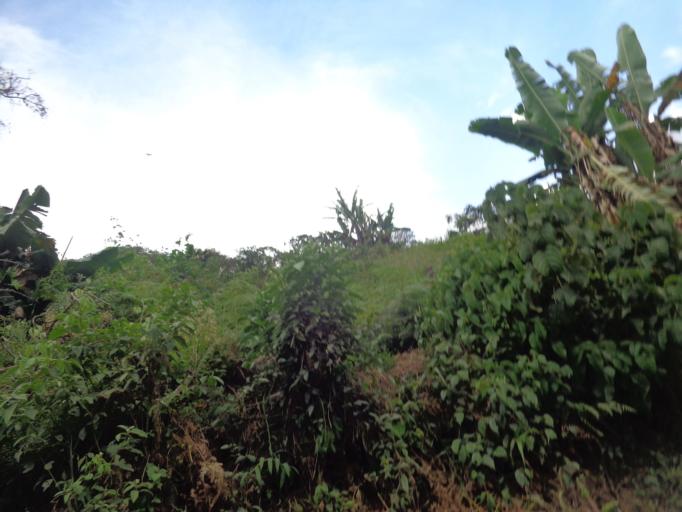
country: BO
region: La Paz
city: Coroico
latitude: -16.1123
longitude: -67.7761
